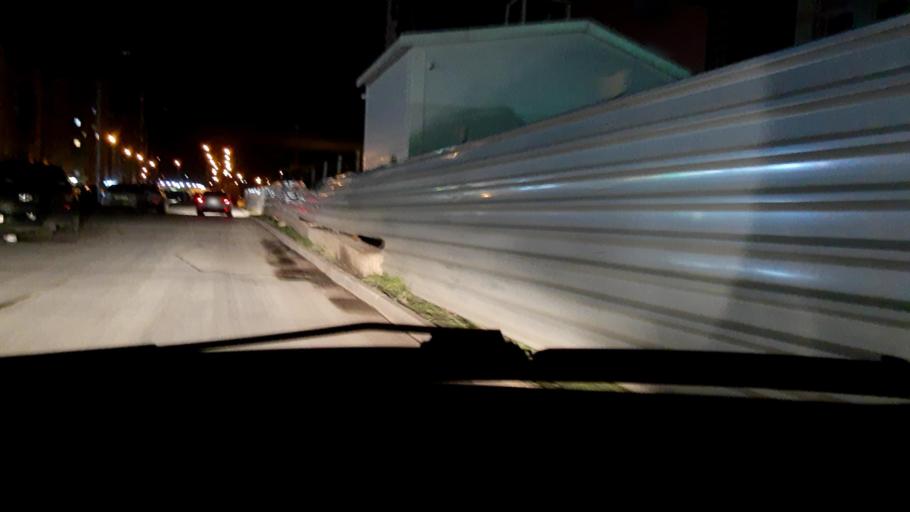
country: RU
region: Bashkortostan
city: Mikhaylovka
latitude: 54.6969
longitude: 55.8578
